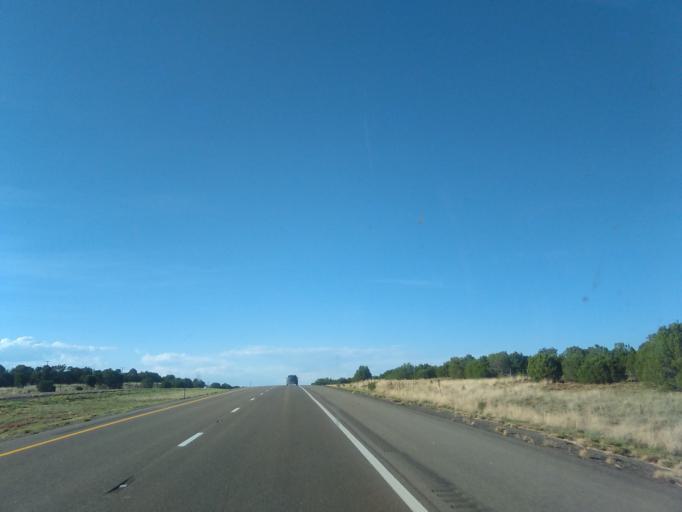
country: US
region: New Mexico
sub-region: San Miguel County
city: Las Vegas
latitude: 35.4756
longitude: -105.2747
